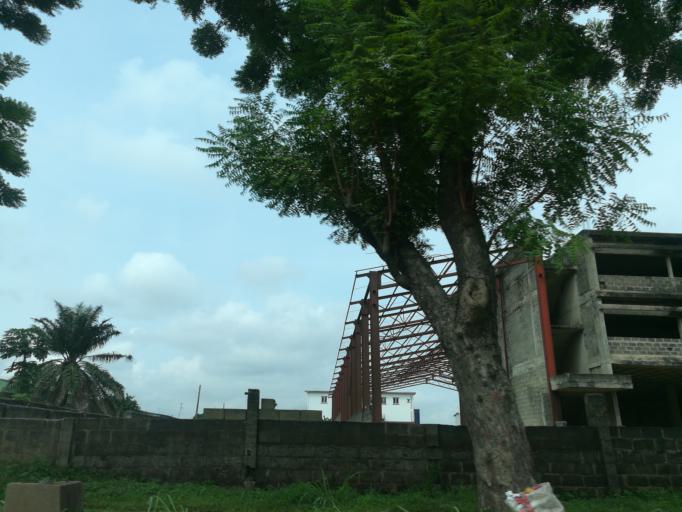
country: NG
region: Lagos
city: Ojota
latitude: 6.6093
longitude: 3.3683
